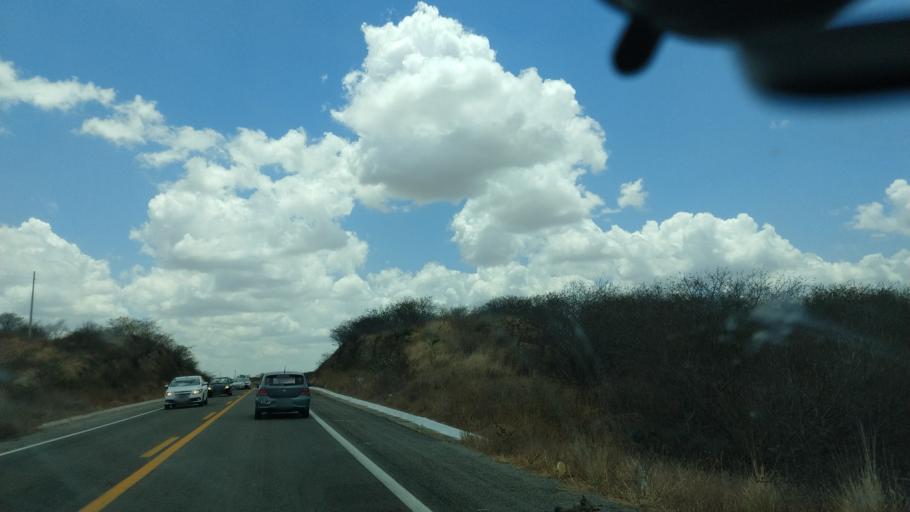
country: BR
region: Rio Grande do Norte
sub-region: Cerro Cora
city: Cerro Cora
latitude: -6.2050
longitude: -36.2795
